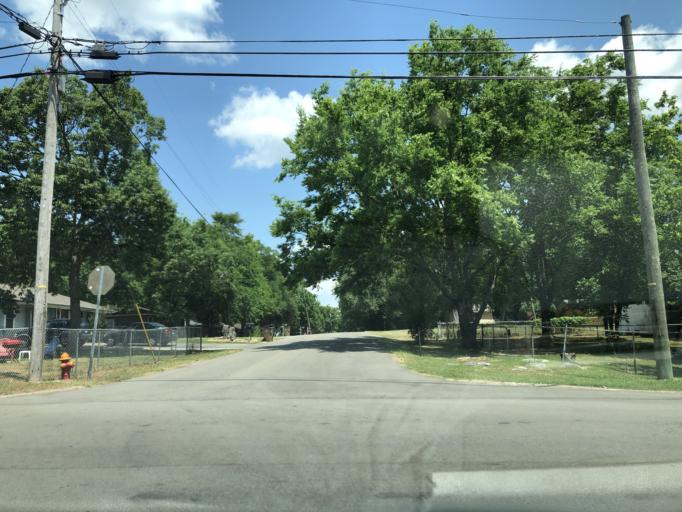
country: US
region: Tennessee
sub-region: Davidson County
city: Goodlettsville
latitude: 36.2705
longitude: -86.7054
